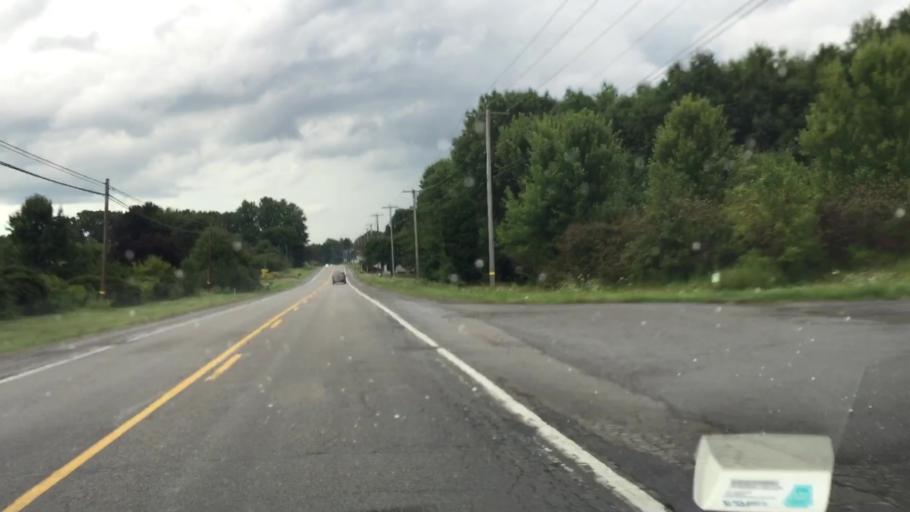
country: US
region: Pennsylvania
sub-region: Butler County
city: Meridian
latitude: 40.8378
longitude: -79.9996
